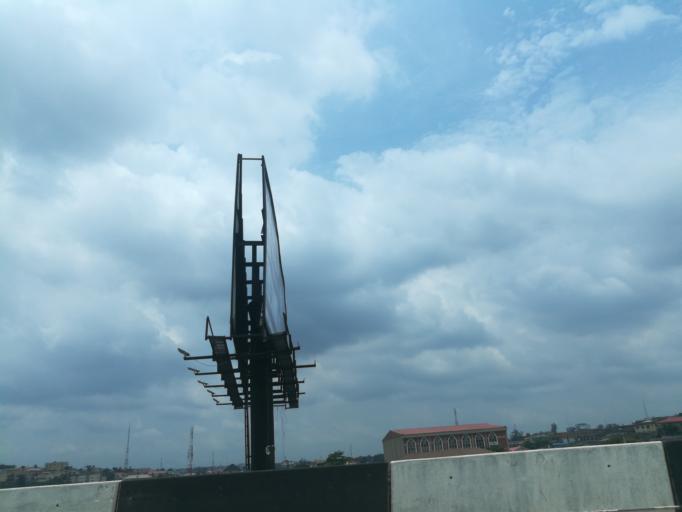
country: NG
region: Lagos
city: Ojota
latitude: 6.5954
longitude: 3.3643
